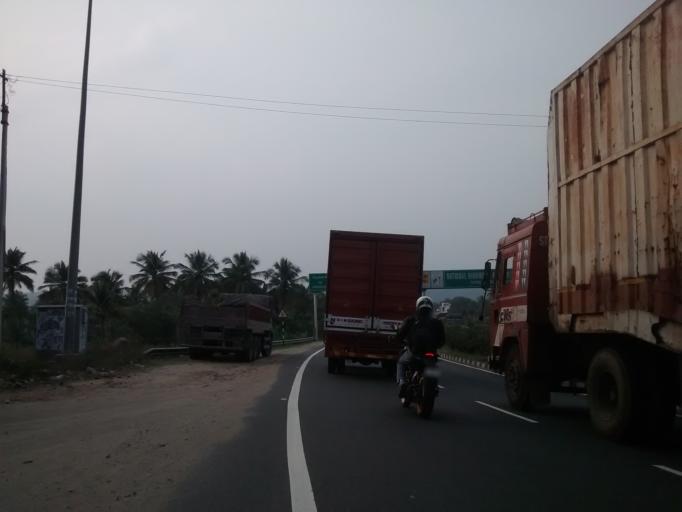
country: IN
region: Tamil Nadu
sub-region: Salem
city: Omalur
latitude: 11.9376
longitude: 78.0531
